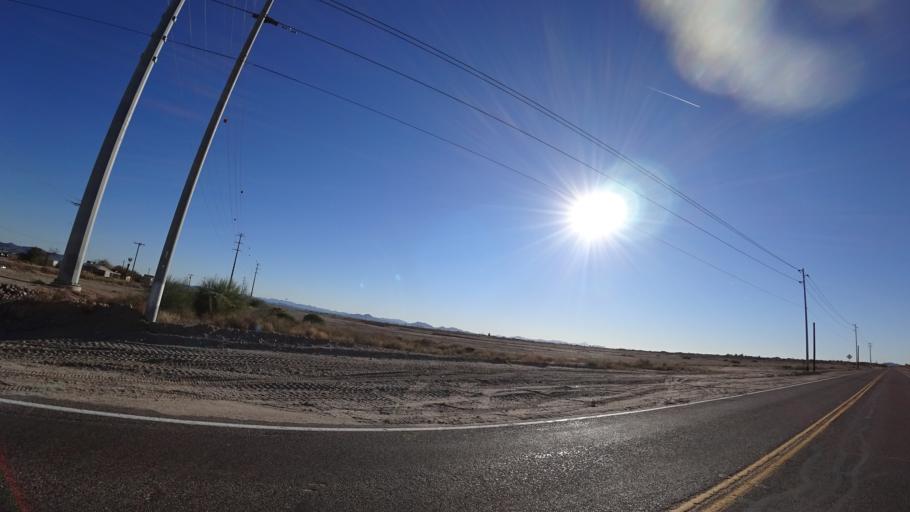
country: US
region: Arizona
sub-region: Maricopa County
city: Citrus Park
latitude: 33.4502
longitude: -112.4618
